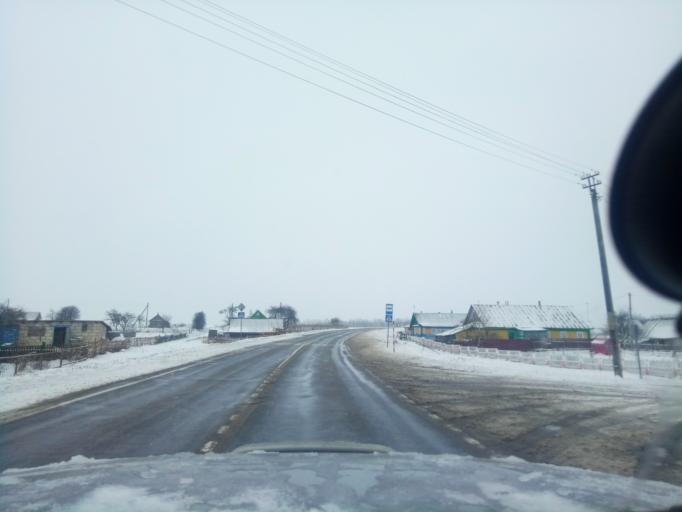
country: BY
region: Minsk
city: Haradzyeya
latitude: 53.3330
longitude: 26.5405
